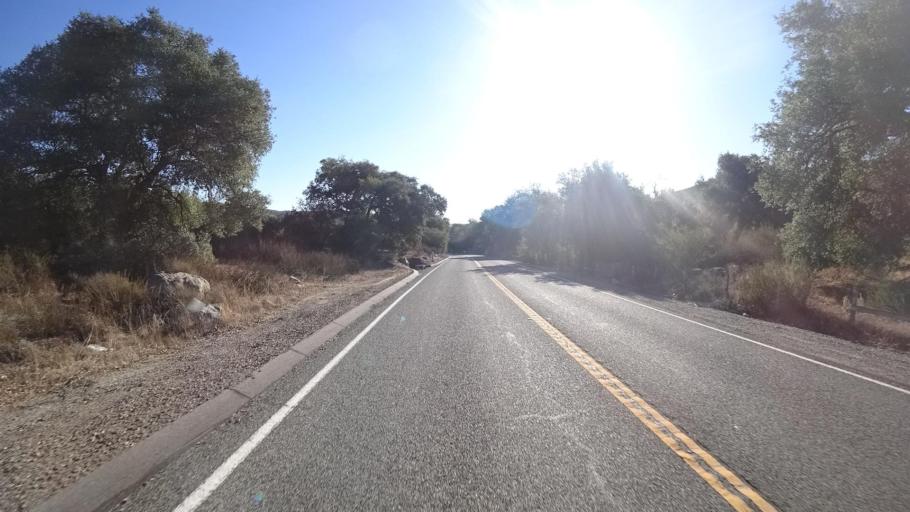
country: MX
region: Baja California
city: Tecate
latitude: 32.5996
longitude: -116.5792
